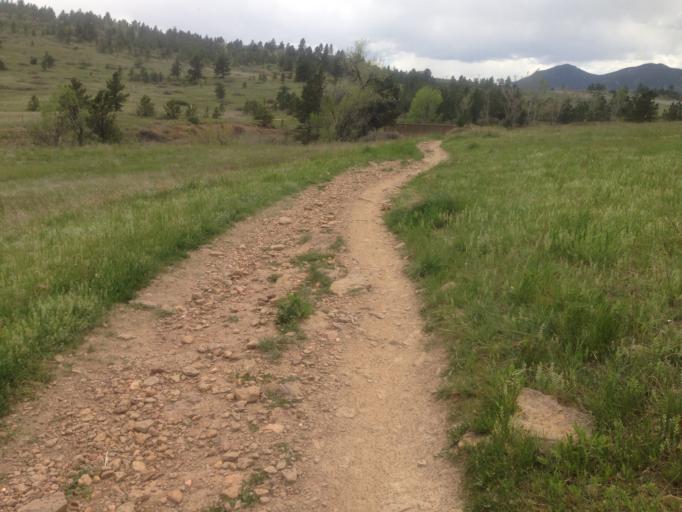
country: US
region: Colorado
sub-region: Boulder County
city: Superior
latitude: 39.9511
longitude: -105.2321
